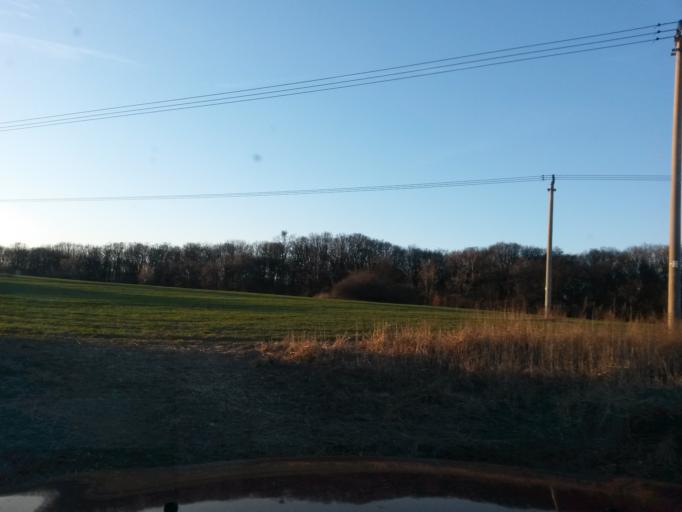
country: SK
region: Kosicky
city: Kosice
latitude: 48.7076
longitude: 21.3090
